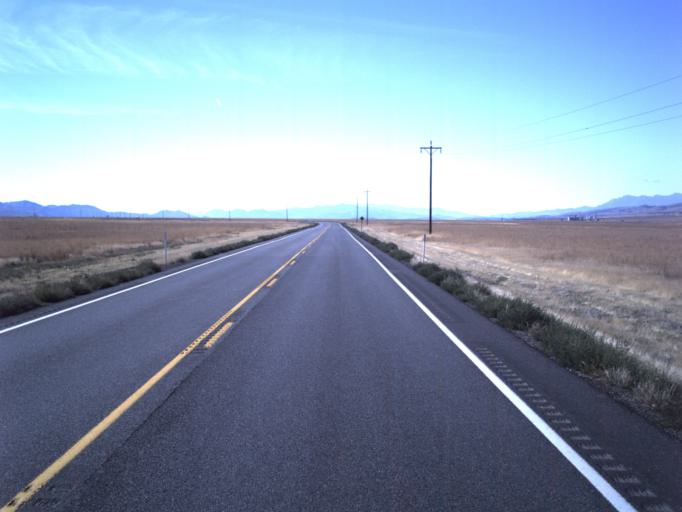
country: US
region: Utah
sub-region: Juab County
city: Nephi
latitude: 39.6496
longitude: -111.8593
